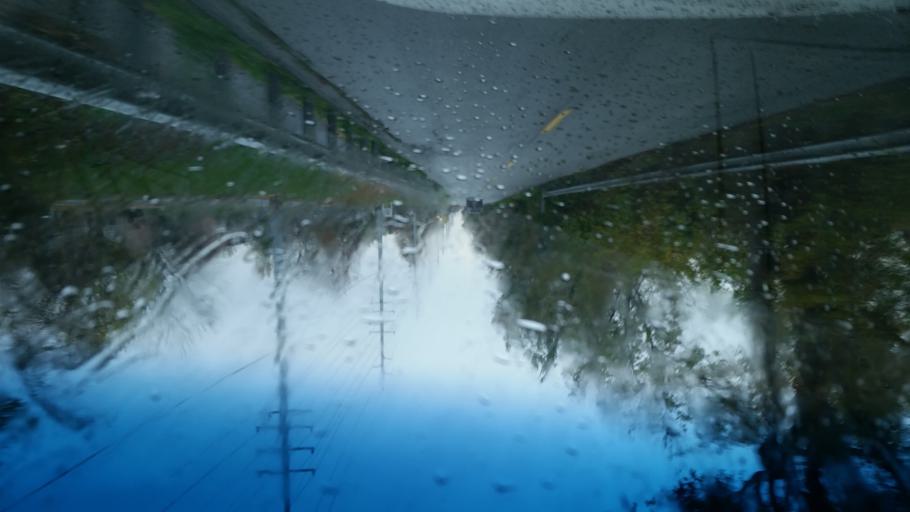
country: US
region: Indiana
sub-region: Howard County
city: Kokomo
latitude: 40.4646
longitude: -86.1460
